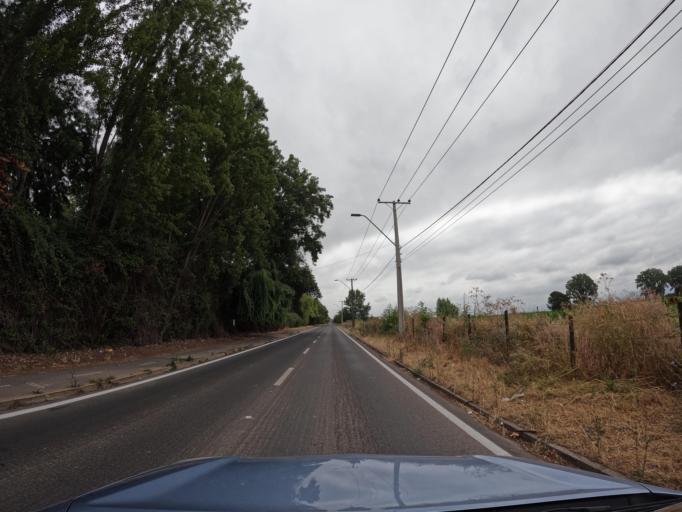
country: CL
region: O'Higgins
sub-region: Provincia de Colchagua
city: Chimbarongo
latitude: -34.7315
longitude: -71.0608
